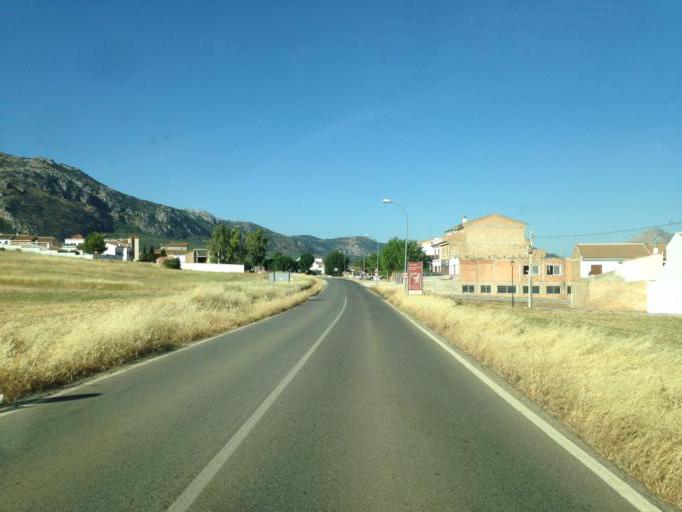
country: ES
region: Andalusia
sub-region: Provincia de Malaga
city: Villanueva del Rosario
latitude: 37.0047
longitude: -4.3646
